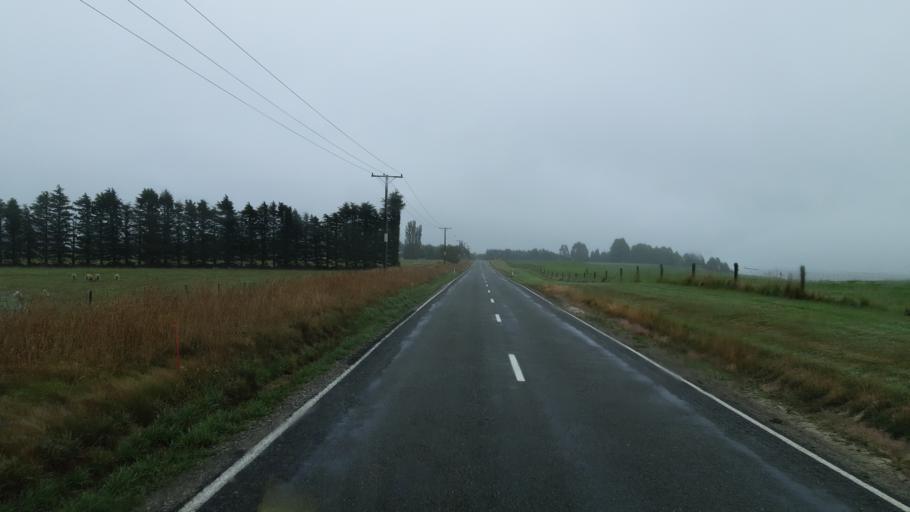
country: NZ
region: Otago
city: Oamaru
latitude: -44.9283
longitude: 170.7985
